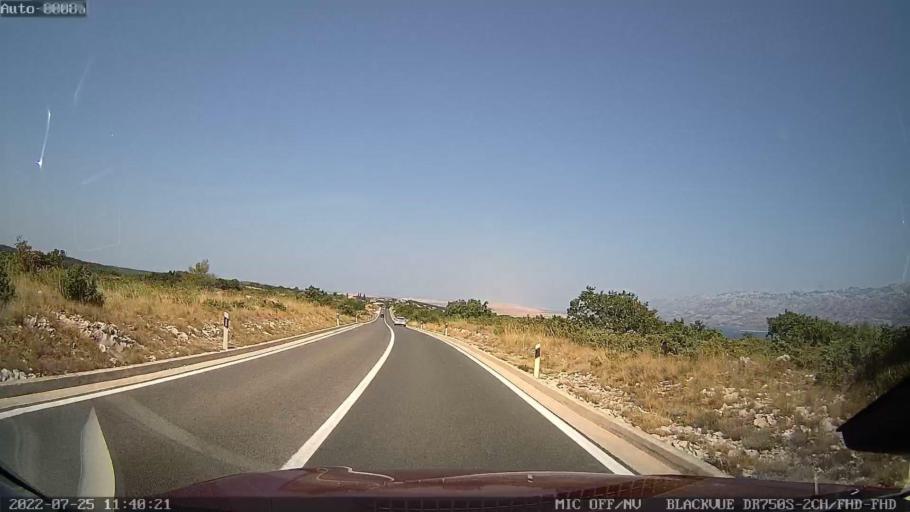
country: HR
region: Zadarska
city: Razanac
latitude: 44.2628
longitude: 15.3616
